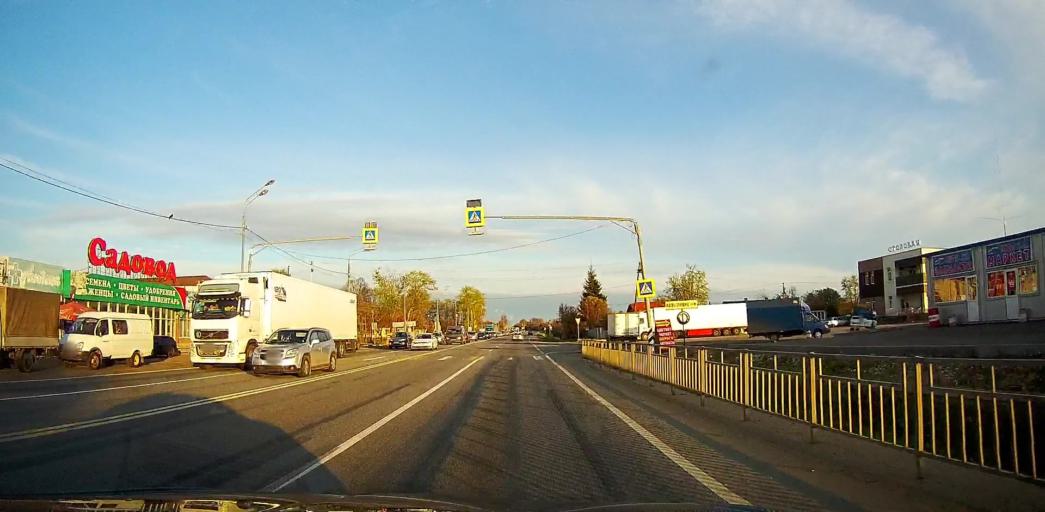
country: RU
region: Moskovskaya
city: Troitskoye
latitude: 55.2483
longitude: 38.5276
